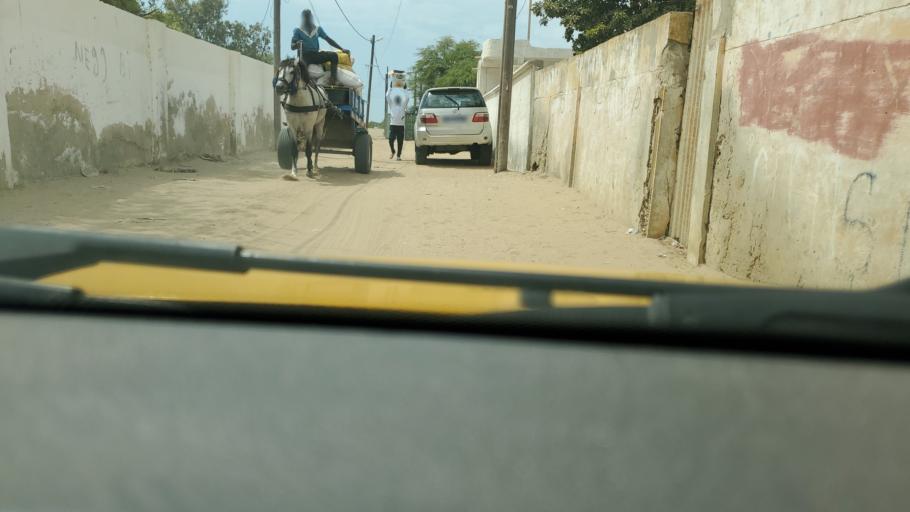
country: SN
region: Saint-Louis
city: Saint-Louis
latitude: 16.0263
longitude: -16.4754
